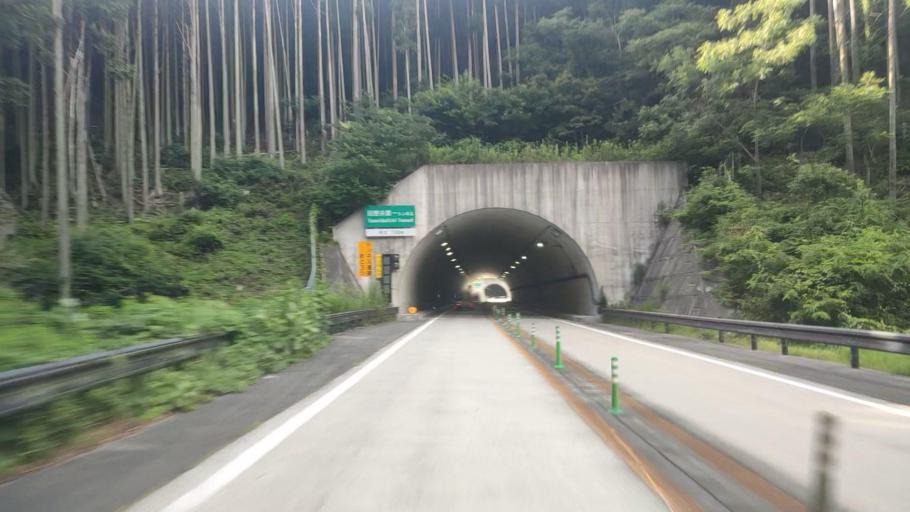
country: JP
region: Wakayama
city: Tanabe
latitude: 33.5971
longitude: 135.4340
